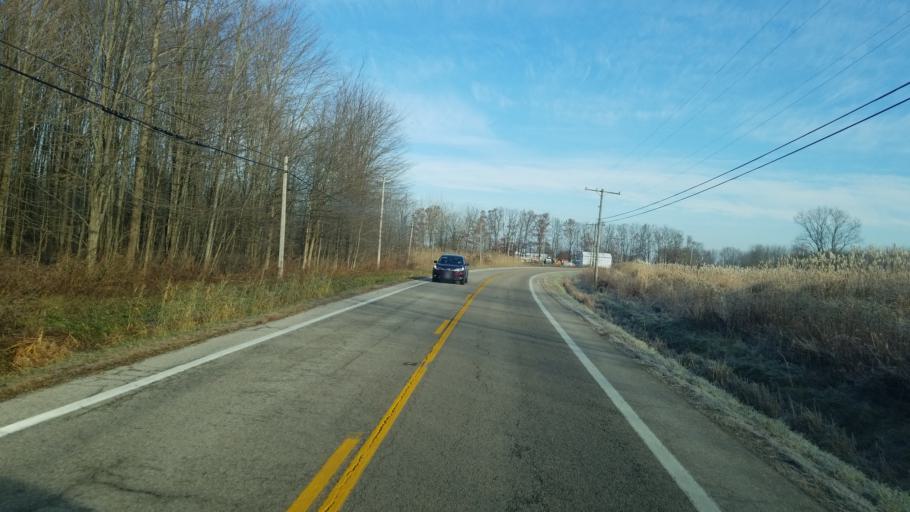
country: US
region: Ohio
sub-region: Ashtabula County
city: Jefferson
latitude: 41.7277
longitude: -80.6690
